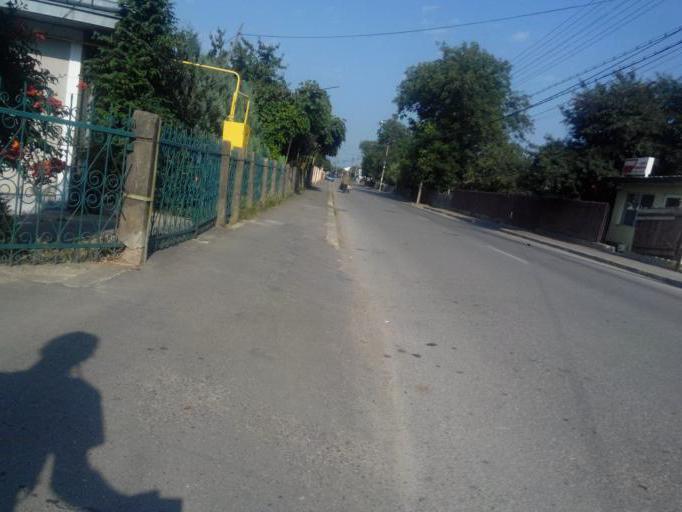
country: RO
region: Suceava
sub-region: Municipiul Falticeni
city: Falticeni
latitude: 47.4674
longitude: 26.2808
